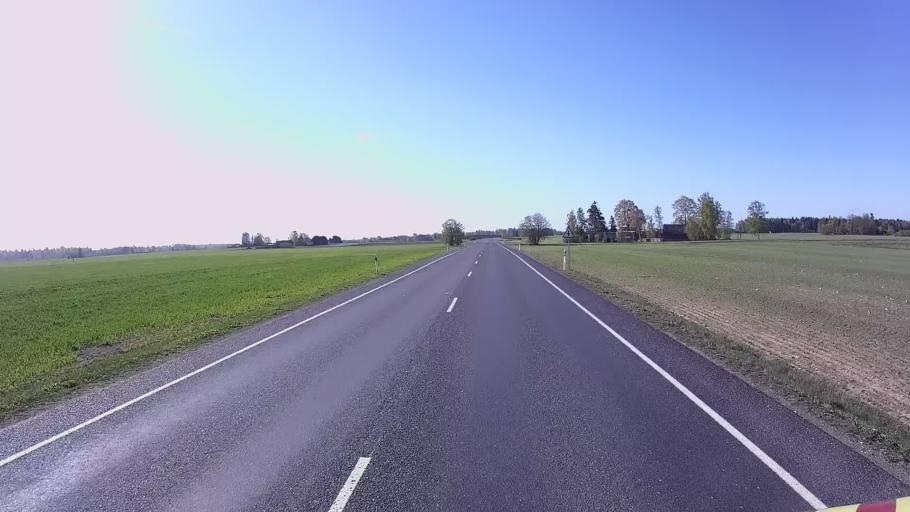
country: EE
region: Viljandimaa
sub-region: Vohma linn
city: Vohma
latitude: 58.7078
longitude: 25.6191
